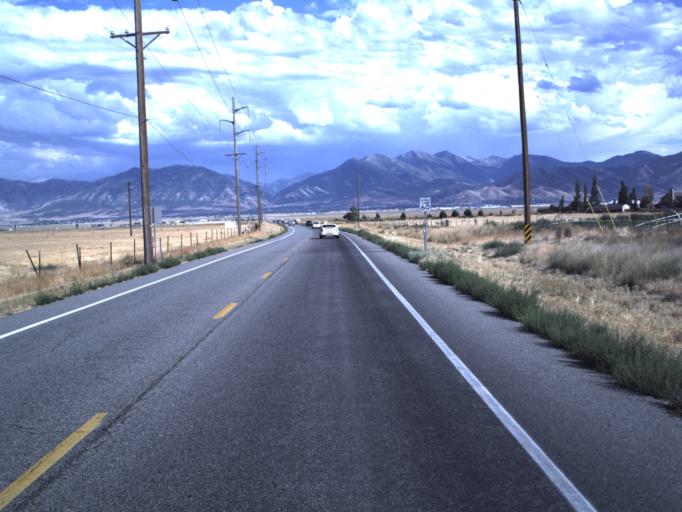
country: US
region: Utah
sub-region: Tooele County
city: Grantsville
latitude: 40.5883
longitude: -112.4155
